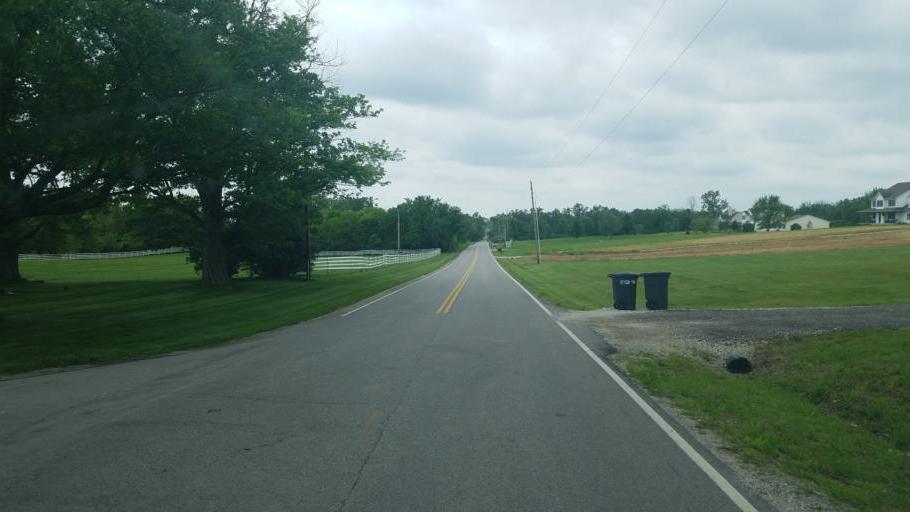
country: US
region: Ohio
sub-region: Licking County
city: Granville South
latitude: 40.0269
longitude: -82.5753
